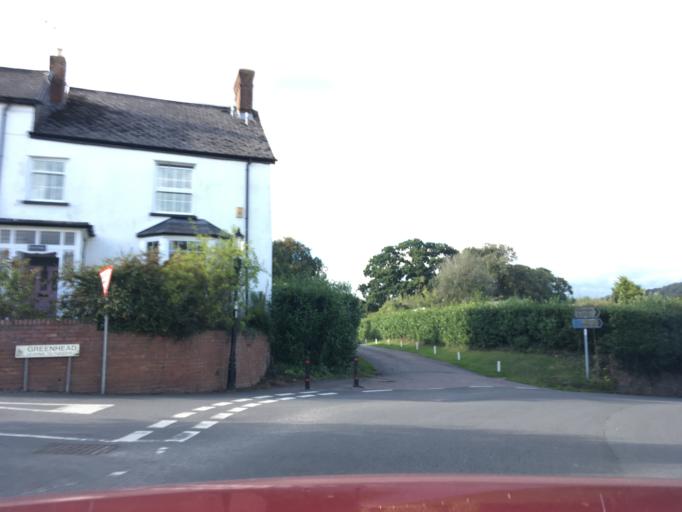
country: GB
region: England
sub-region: Devon
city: Sidmouth
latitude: 50.7178
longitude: -3.2225
